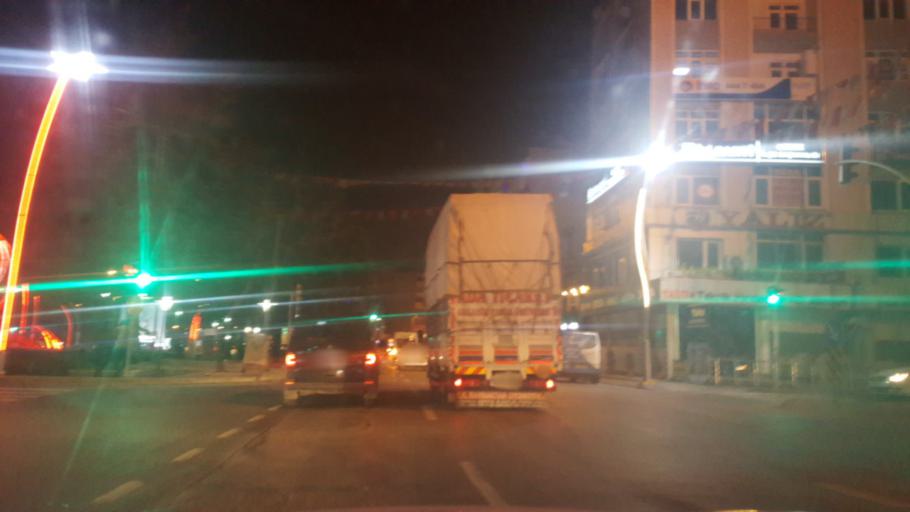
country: TR
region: Kocaeli
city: Gebze
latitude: 40.7976
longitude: 29.4408
